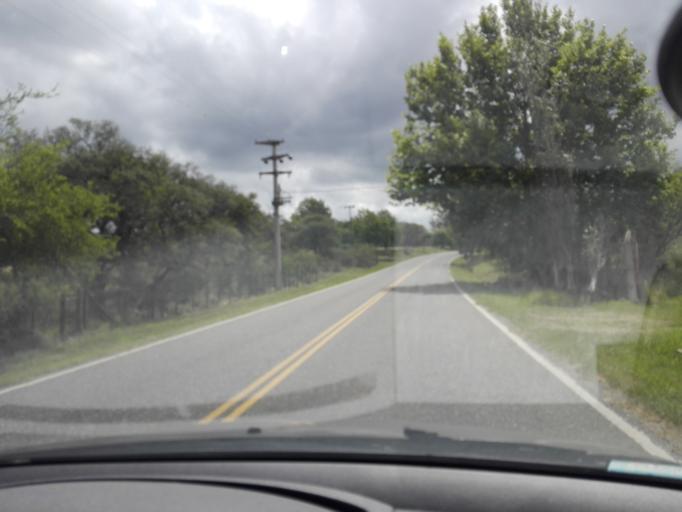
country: AR
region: Cordoba
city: Alta Gracia
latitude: -31.5875
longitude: -64.4723
